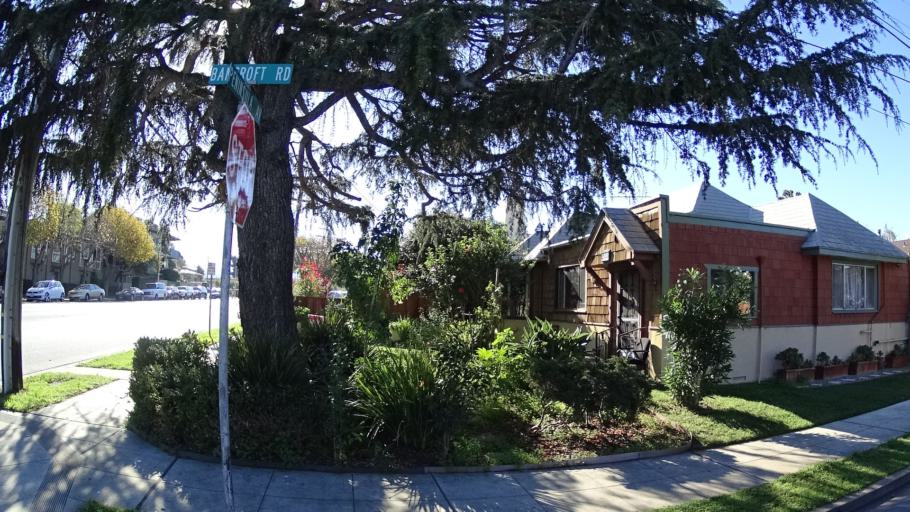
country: US
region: California
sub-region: San Mateo County
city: San Mateo
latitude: 37.5820
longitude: -122.3325
